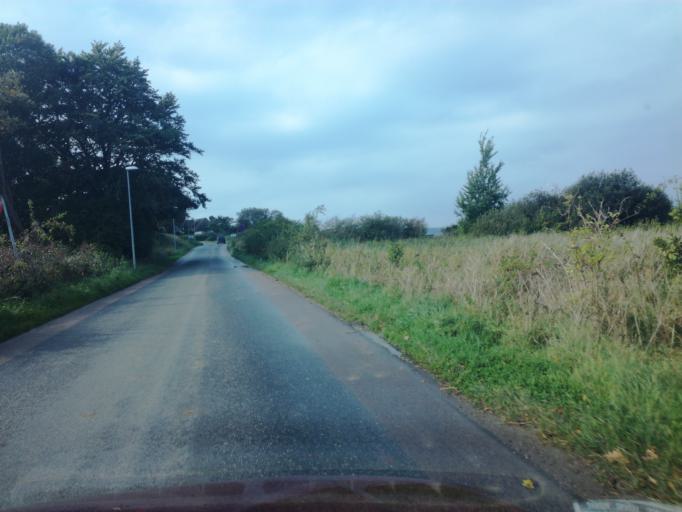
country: DK
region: South Denmark
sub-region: Fredericia Kommune
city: Fredericia
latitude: 55.6248
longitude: 9.7970
